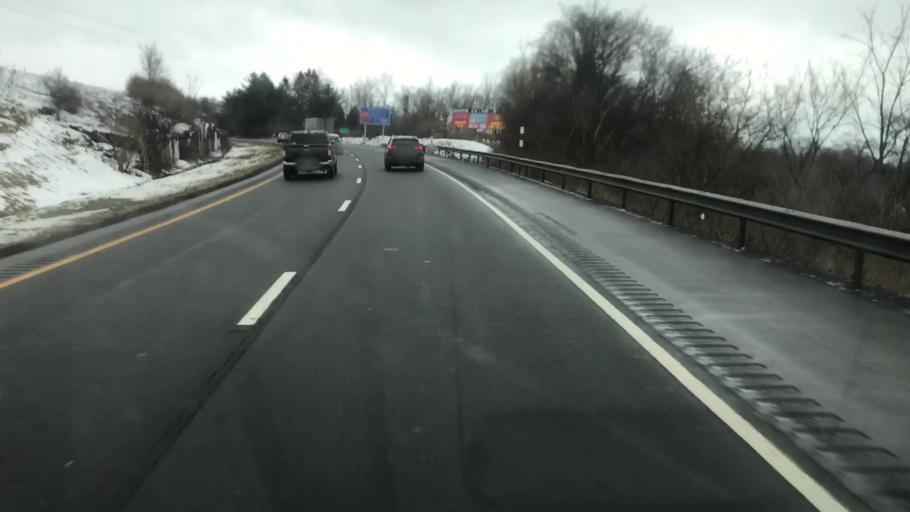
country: US
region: New York
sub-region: Cortland County
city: Cortland
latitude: 42.6143
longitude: -76.1816
